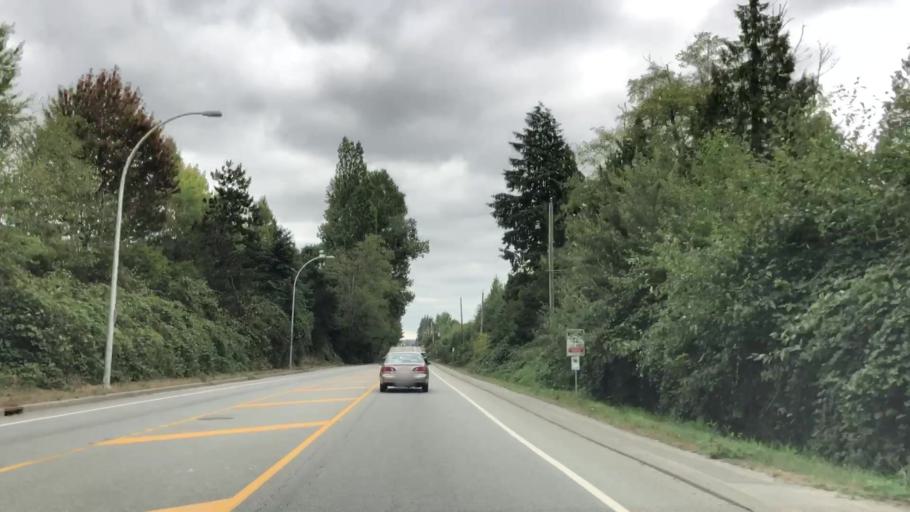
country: CA
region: British Columbia
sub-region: Greater Vancouver Regional District
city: White Rock
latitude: 49.0601
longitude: -122.7779
